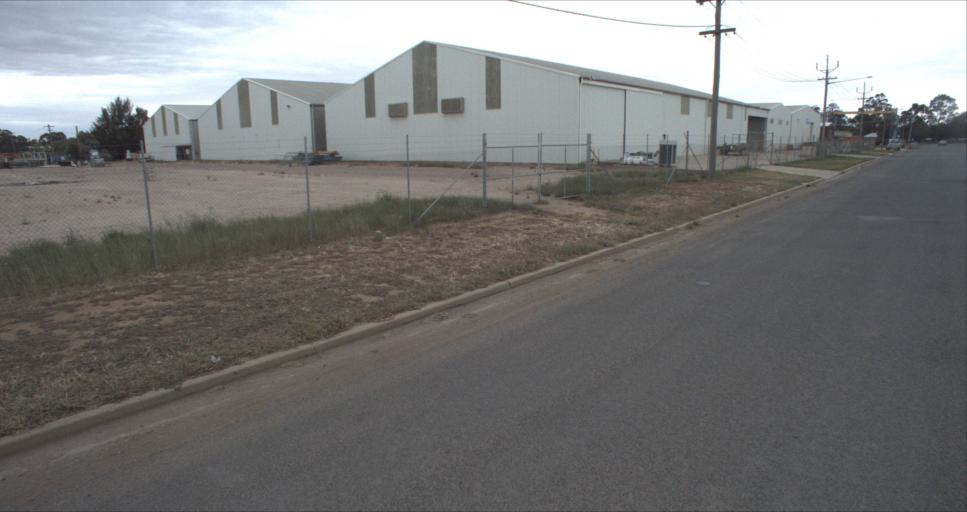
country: AU
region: New South Wales
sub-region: Leeton
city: Leeton
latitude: -34.5479
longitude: 146.3875
